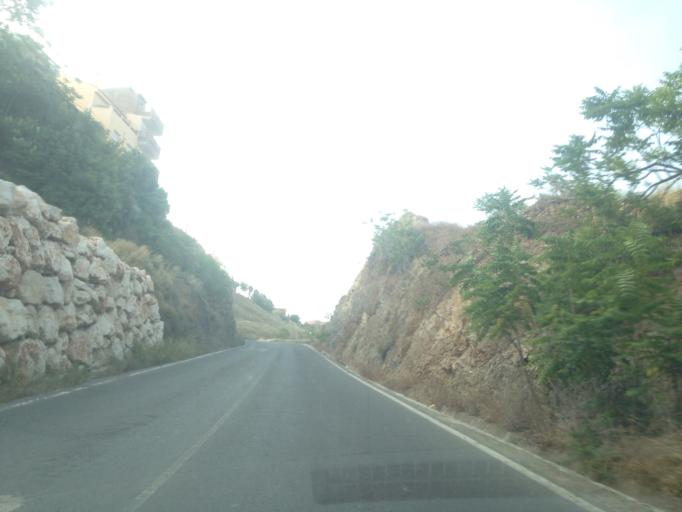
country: ES
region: Andalusia
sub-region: Provincia de Malaga
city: Malaga
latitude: 36.7397
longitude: -4.4120
